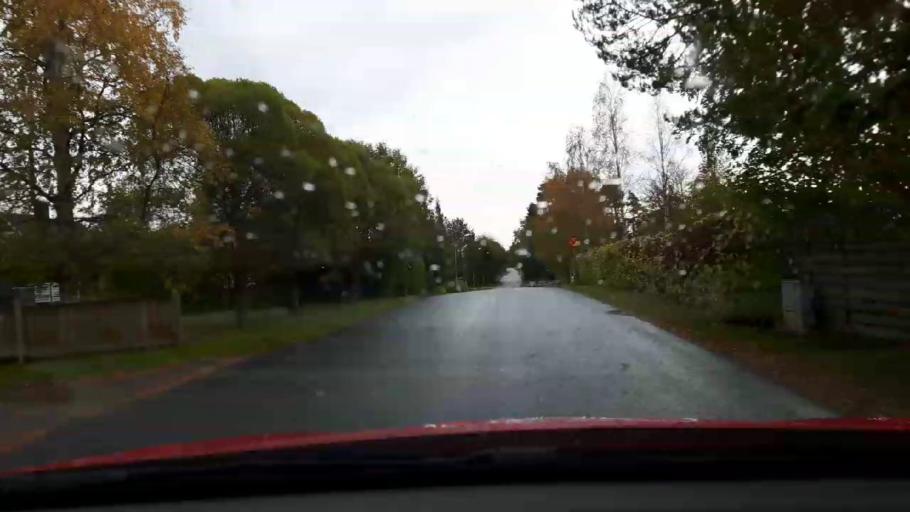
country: SE
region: Jaemtland
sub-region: Bergs Kommun
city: Hoverberg
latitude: 62.9283
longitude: 14.5160
